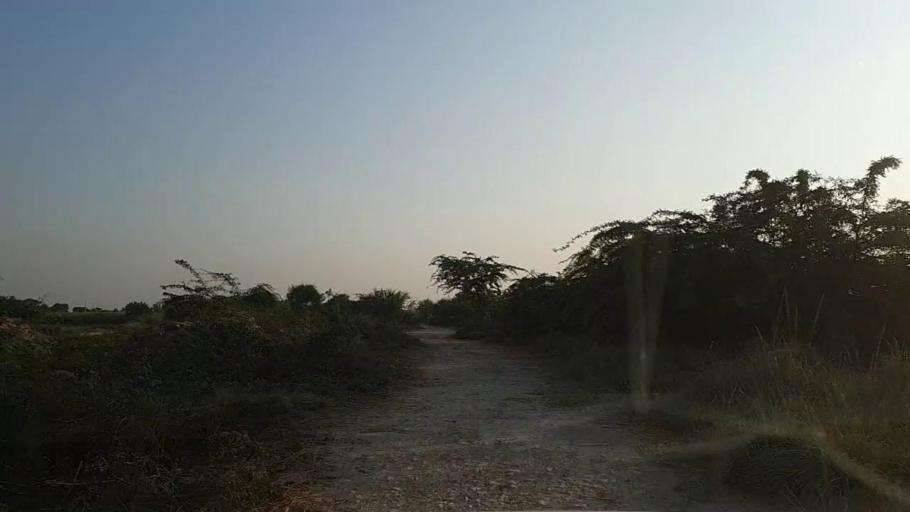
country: PK
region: Sindh
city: Daro Mehar
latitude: 24.7536
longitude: 68.1862
